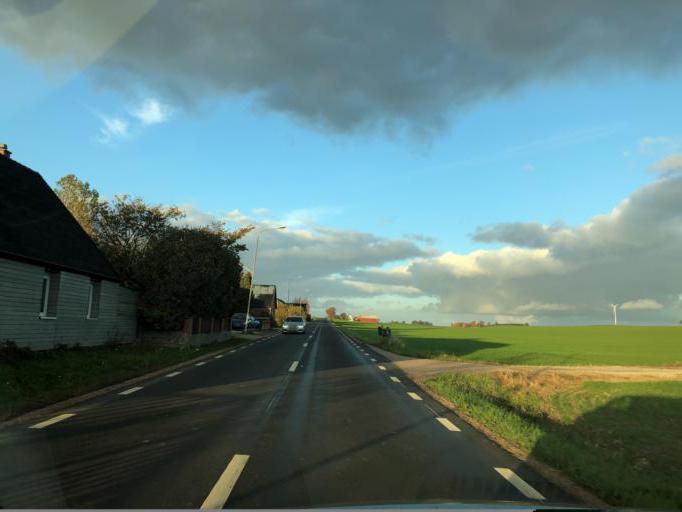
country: SE
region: Skane
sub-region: Svalovs Kommun
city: Svaloev
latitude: 55.8807
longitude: 13.1672
